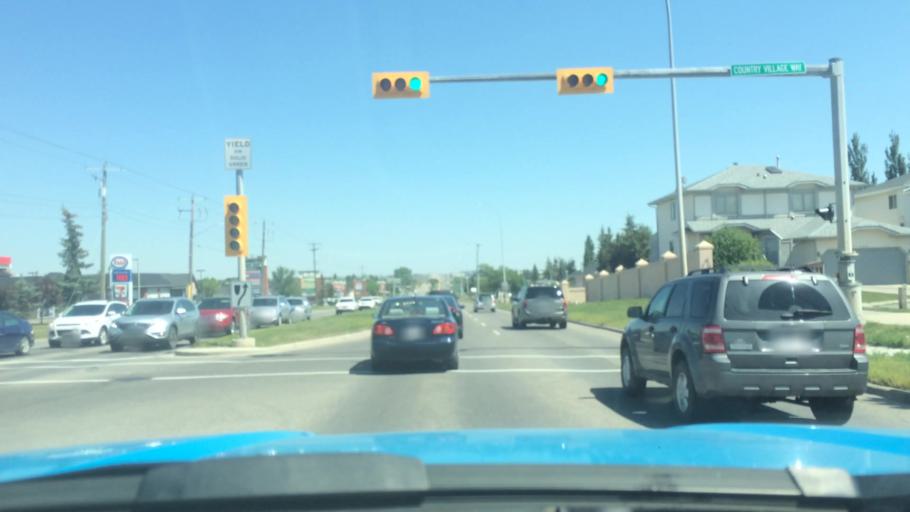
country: CA
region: Alberta
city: Calgary
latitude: 51.1541
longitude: -114.0611
